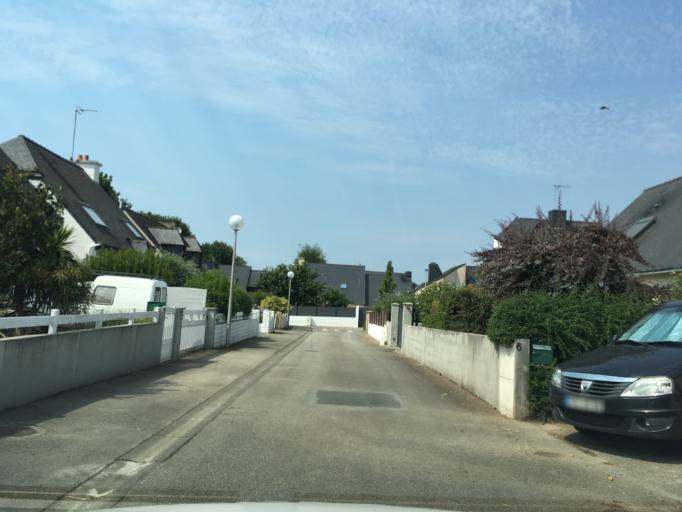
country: FR
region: Brittany
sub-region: Departement du Morbihan
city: Lorient
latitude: 47.7548
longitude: -3.3965
